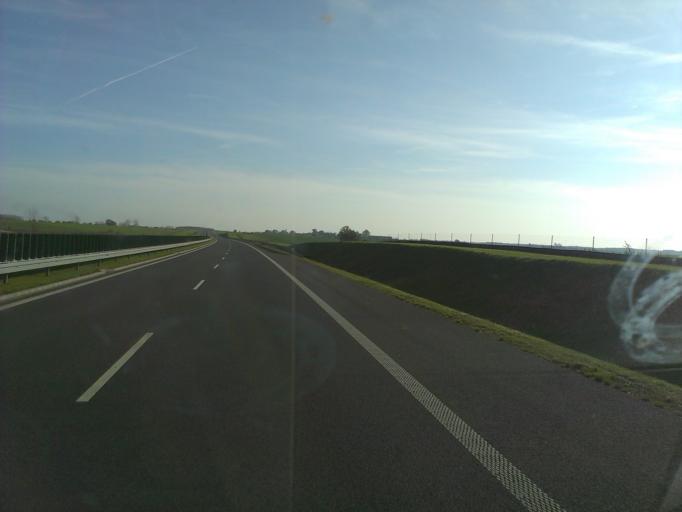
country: PL
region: West Pomeranian Voivodeship
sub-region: Powiat pyrzycki
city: Kozielice
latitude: 53.1021
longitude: 14.7779
